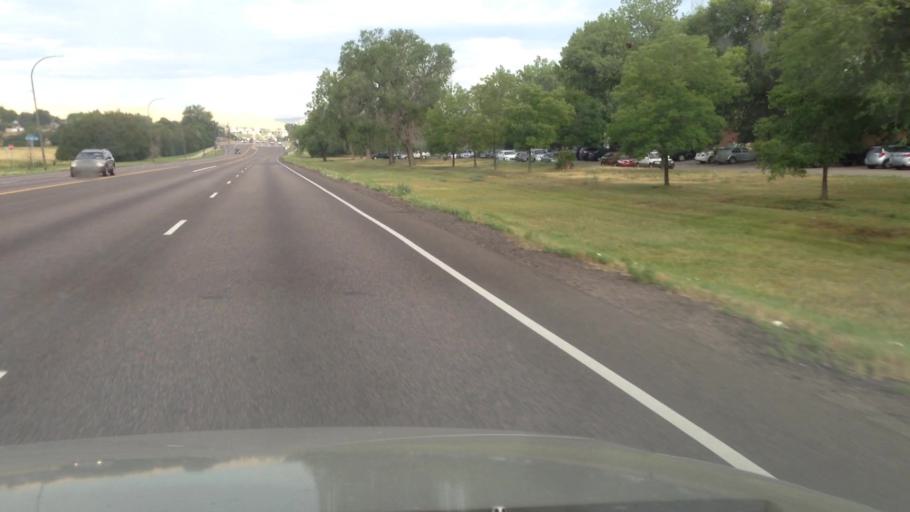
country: US
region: Colorado
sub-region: Jefferson County
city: Lakewood
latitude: 39.7110
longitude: -105.1029
